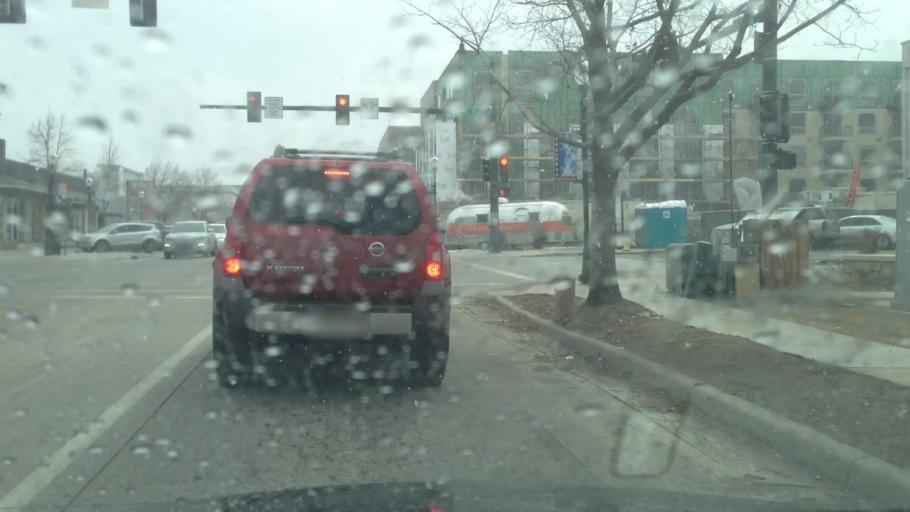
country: US
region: Colorado
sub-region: Douglas County
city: Castle Rock
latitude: 39.3725
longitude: -104.8601
